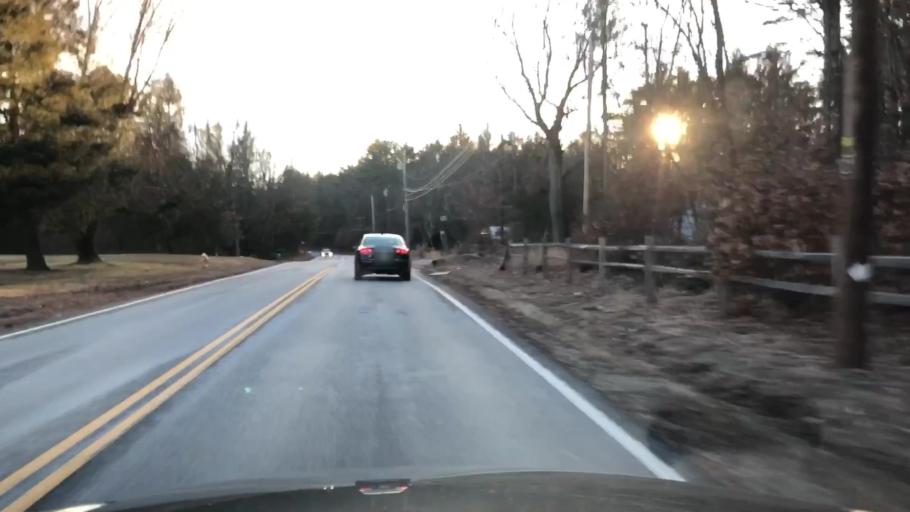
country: US
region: Massachusetts
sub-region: Middlesex County
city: Townsend
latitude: 42.6828
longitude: -71.6962
